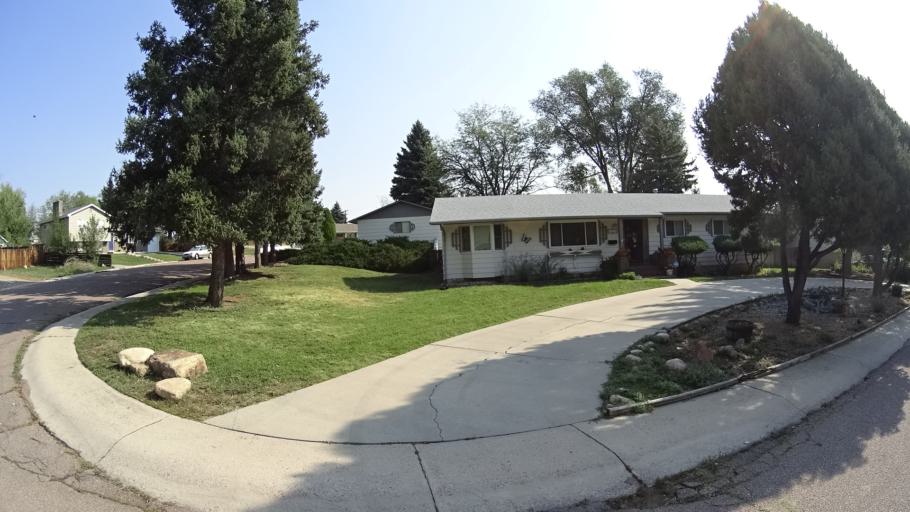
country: US
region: Colorado
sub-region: El Paso County
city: Colorado Springs
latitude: 38.8071
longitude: -104.8379
